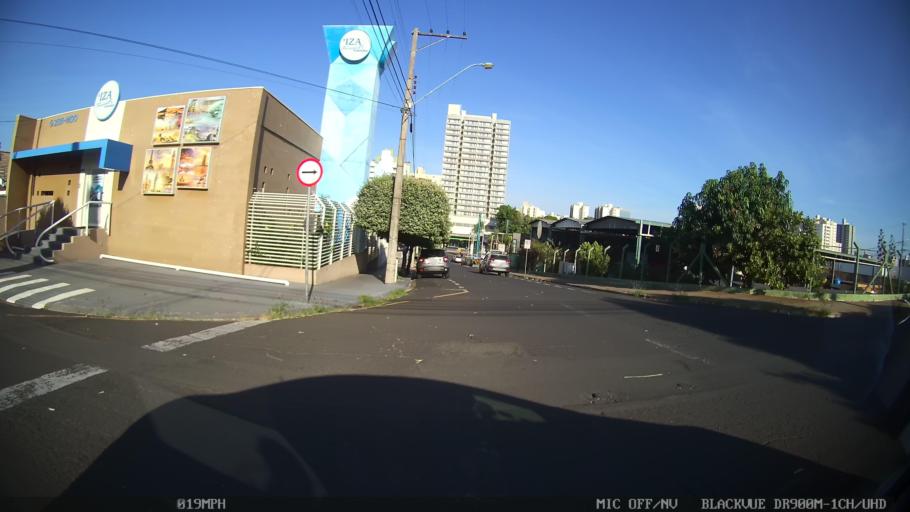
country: BR
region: Sao Paulo
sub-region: Sao Jose Do Rio Preto
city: Sao Jose do Rio Preto
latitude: -20.8168
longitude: -49.3959
